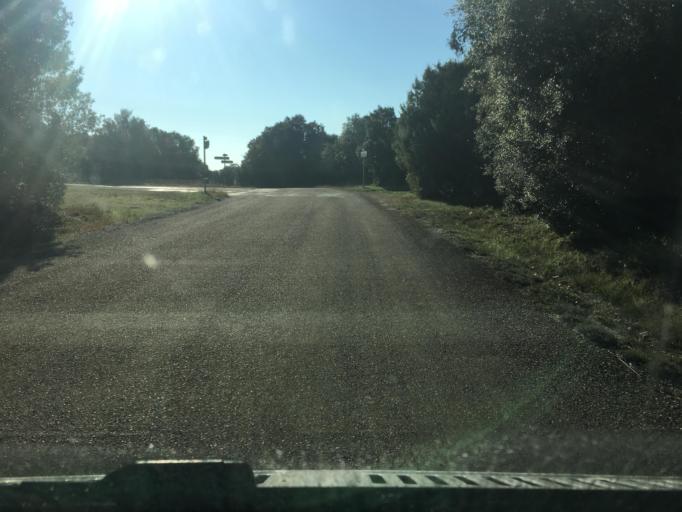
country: FR
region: Languedoc-Roussillon
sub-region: Departement du Gard
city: Goudargues
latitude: 44.1694
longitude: 4.3475
